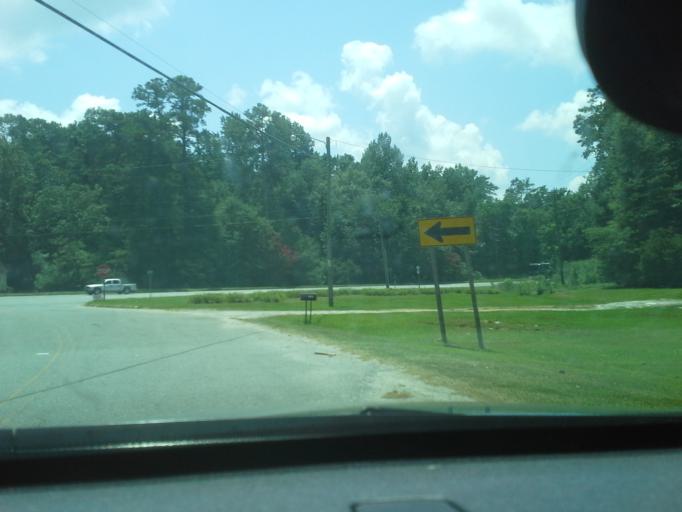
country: US
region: North Carolina
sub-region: Washington County
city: Plymouth
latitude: 35.8377
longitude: -76.7631
